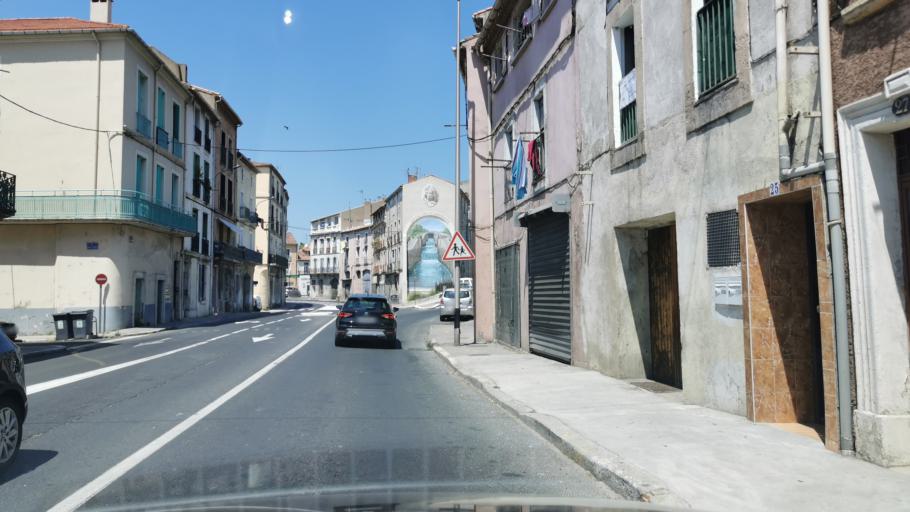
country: FR
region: Languedoc-Roussillon
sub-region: Departement de l'Herault
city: Beziers
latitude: 43.3384
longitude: 3.2122
